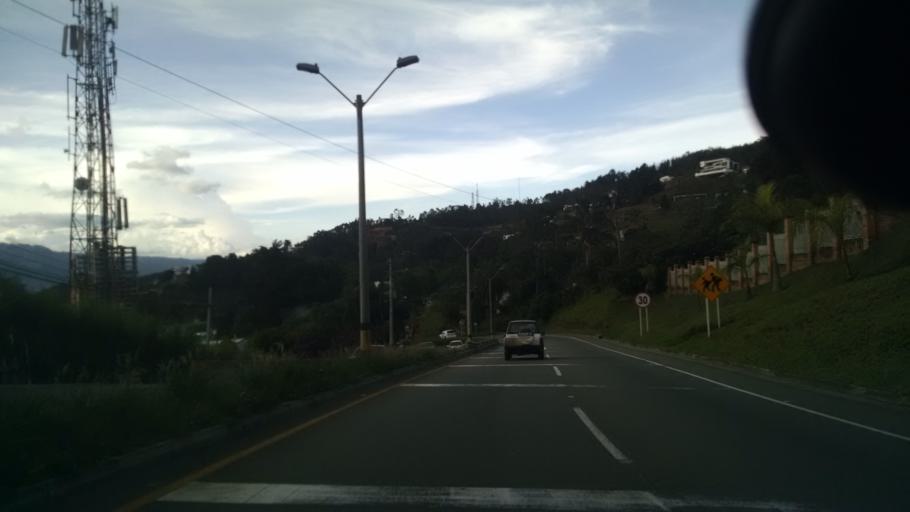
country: CO
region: Antioquia
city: Medellin
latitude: 6.2077
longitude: -75.5457
